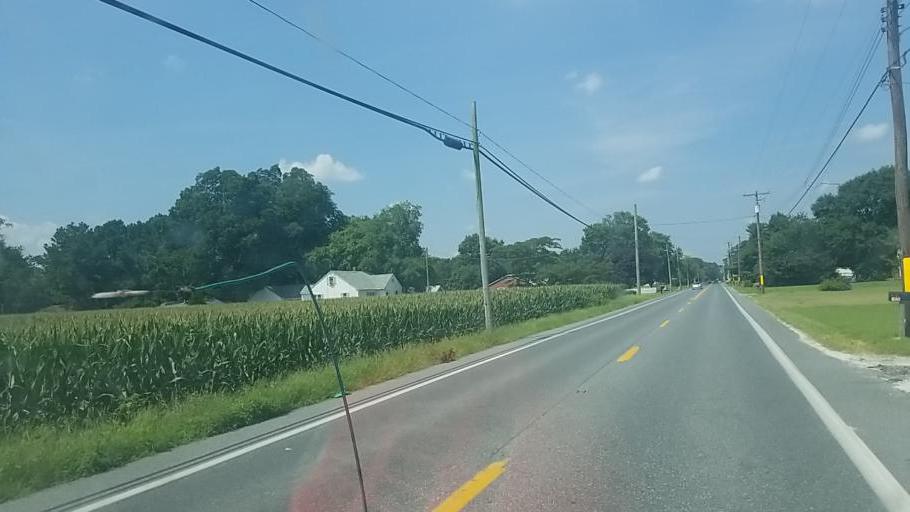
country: US
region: Maryland
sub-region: Wicomico County
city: Salisbury
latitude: 38.3586
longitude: -75.5444
